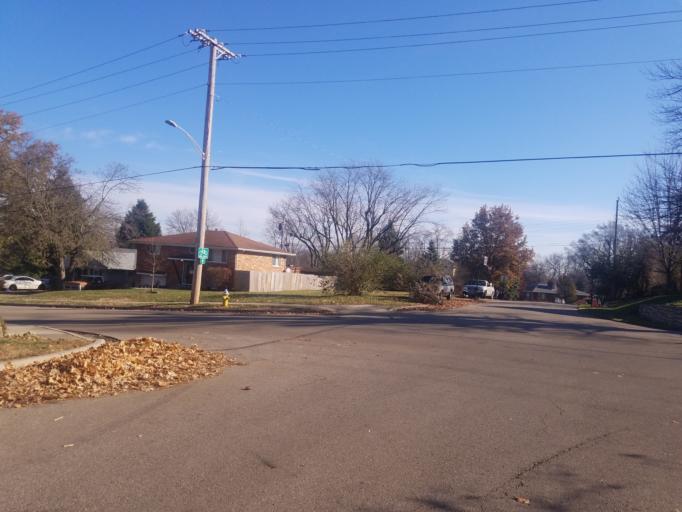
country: US
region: Ohio
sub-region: Montgomery County
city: Kettering
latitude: 39.7081
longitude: -84.1522
